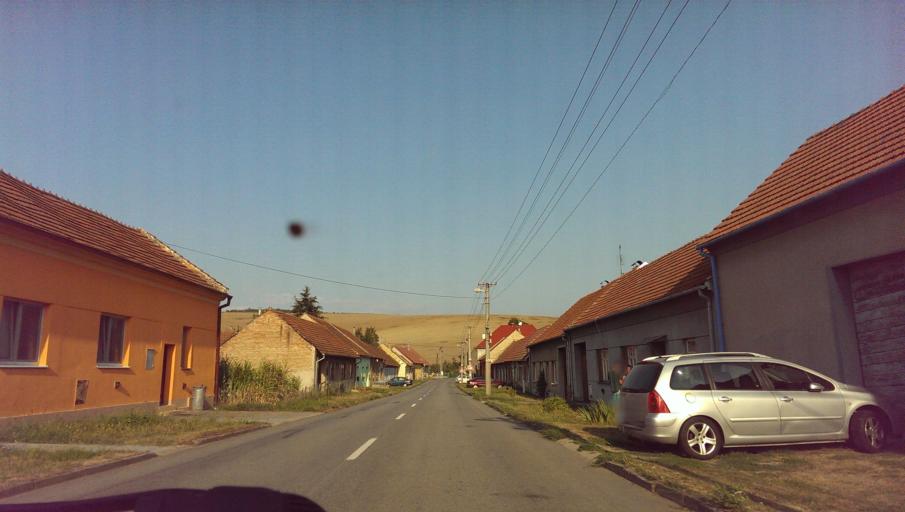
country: CZ
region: Zlin
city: Korycany
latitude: 49.1101
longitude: 17.1386
